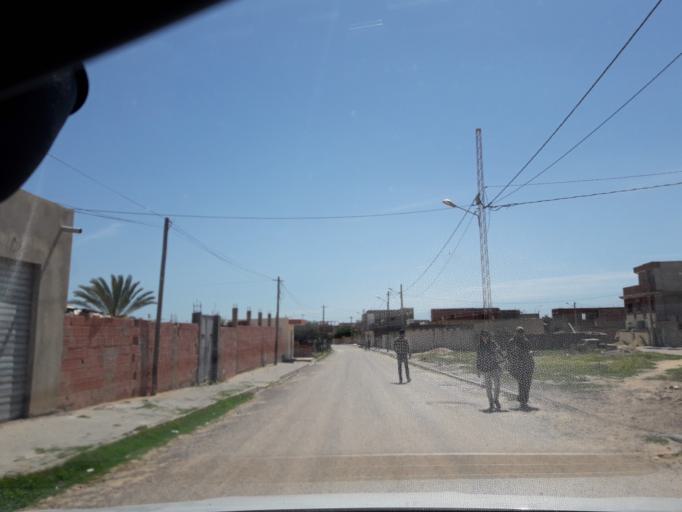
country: TN
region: Safaqis
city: Sfax
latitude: 34.7428
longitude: 10.5193
